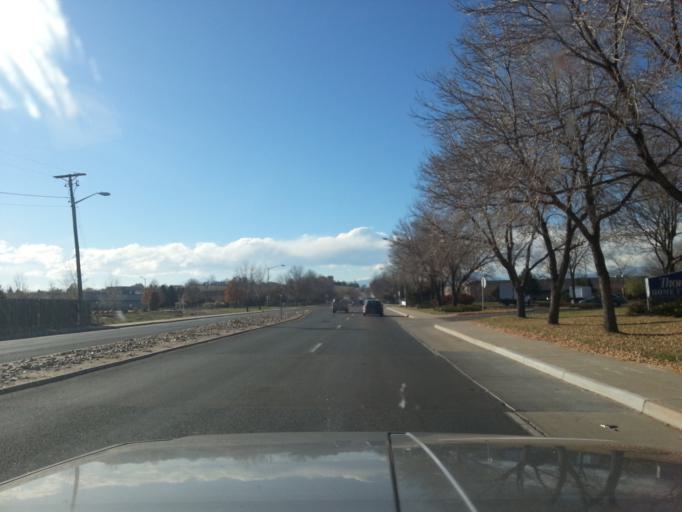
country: US
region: Colorado
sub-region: Larimer County
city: Loveland
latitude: 40.3784
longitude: -105.0765
